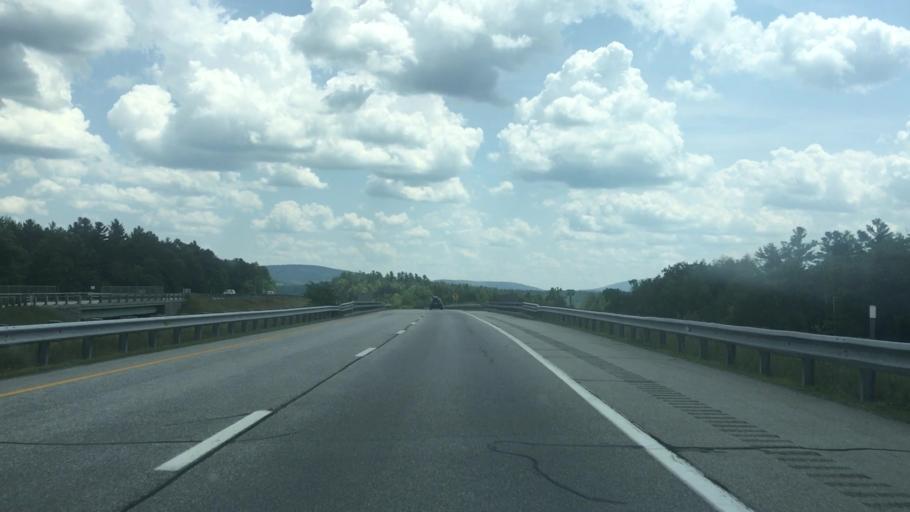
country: US
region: New Hampshire
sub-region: Merrimack County
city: New London
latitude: 43.4231
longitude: -72.0381
